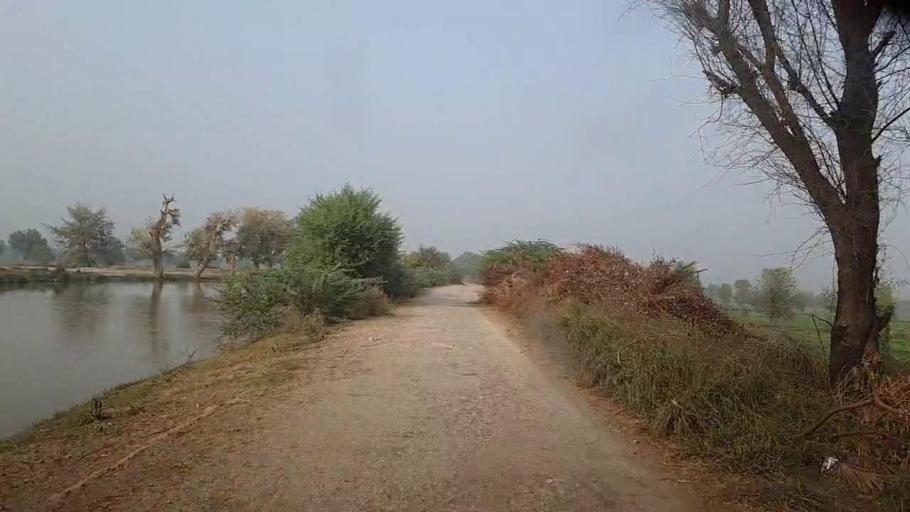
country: PK
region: Sindh
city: Bozdar
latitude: 27.1597
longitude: 68.6604
